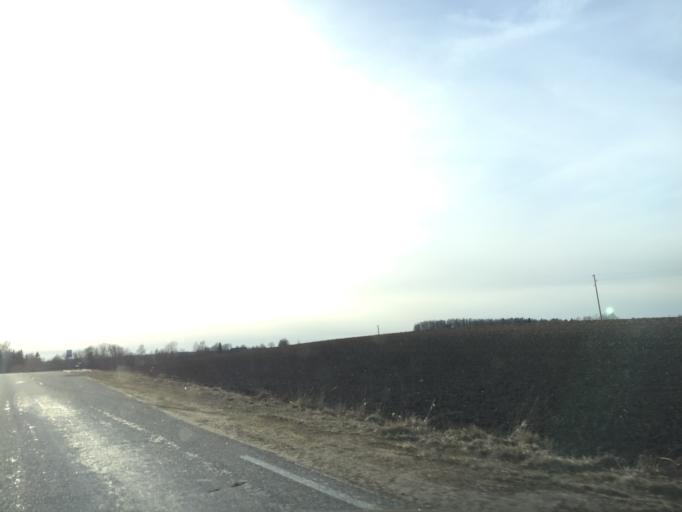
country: LV
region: Sigulda
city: Sigulda
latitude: 57.1644
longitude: 24.8007
